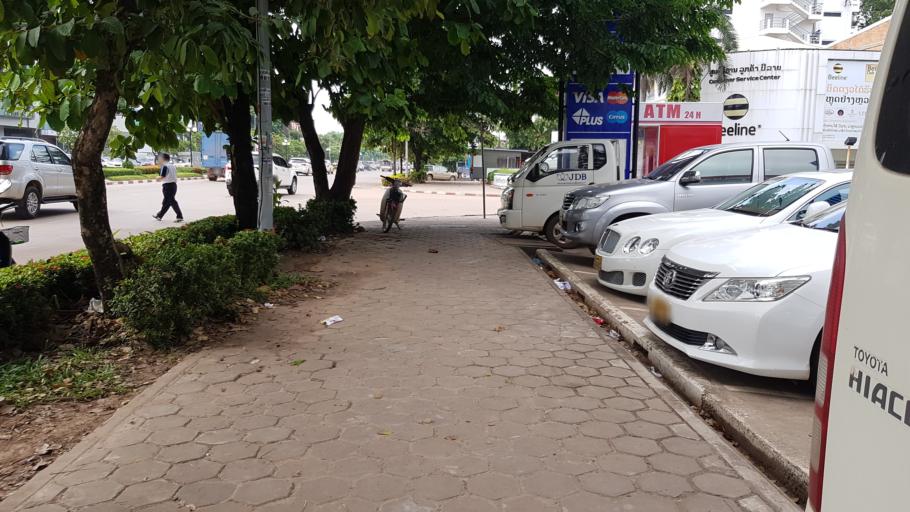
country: LA
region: Vientiane
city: Vientiane
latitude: 17.9667
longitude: 102.6142
